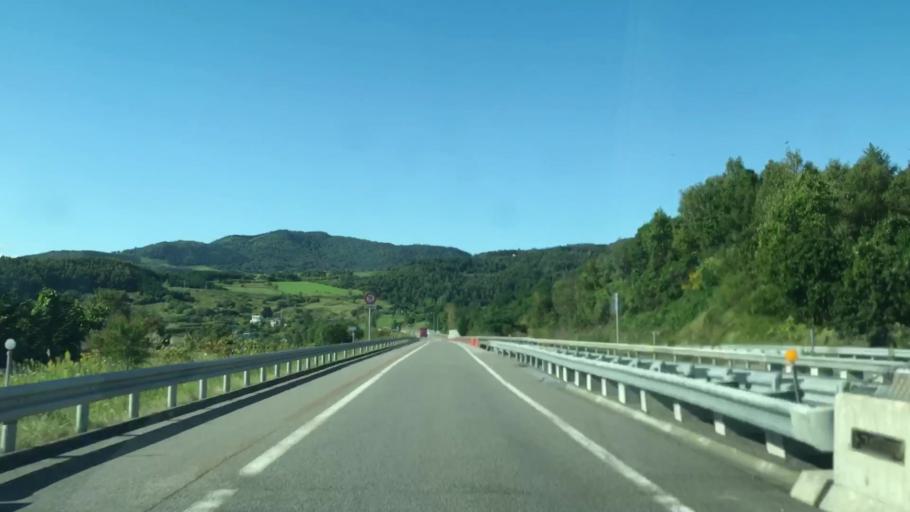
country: JP
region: Hokkaido
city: Date
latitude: 42.5438
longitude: 140.7936
